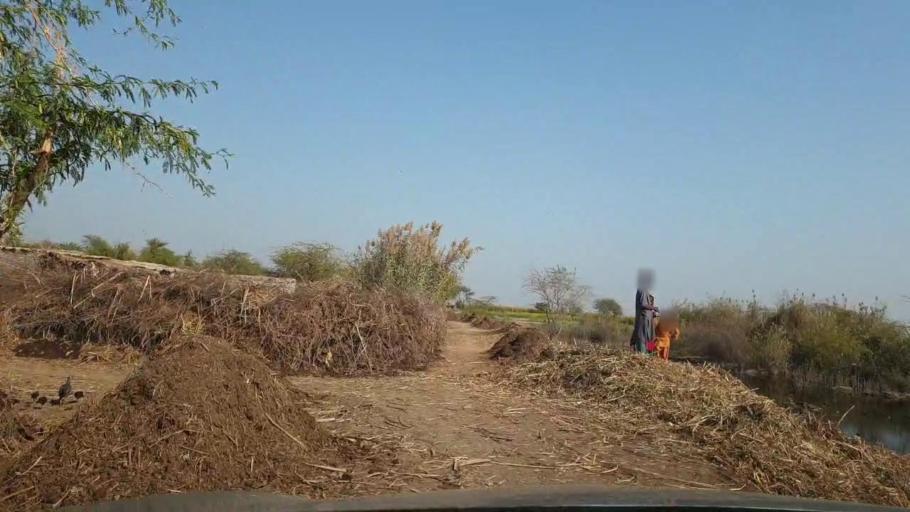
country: PK
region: Sindh
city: Berani
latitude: 25.6441
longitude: 68.8275
